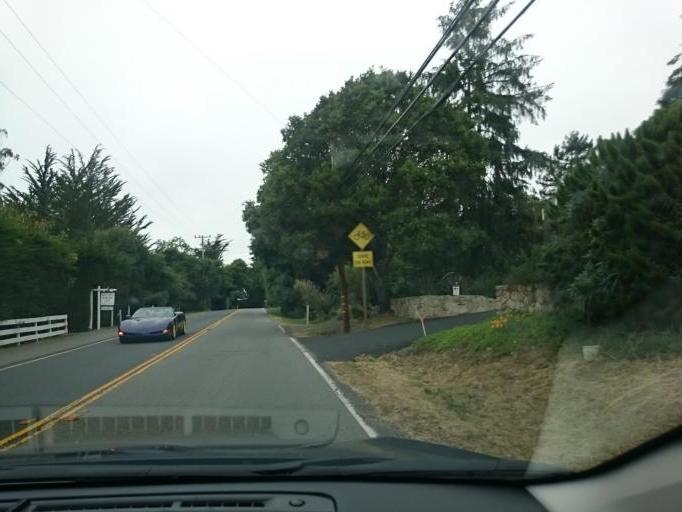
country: US
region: California
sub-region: Marin County
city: Inverness
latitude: 38.0735
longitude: -122.8014
